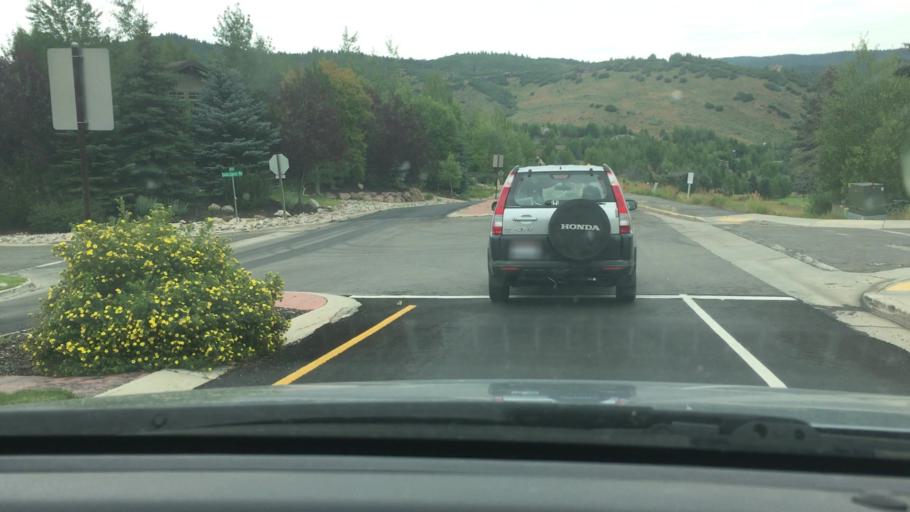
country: US
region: Utah
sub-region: Summit County
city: Summit Park
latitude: 40.7592
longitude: -111.5745
